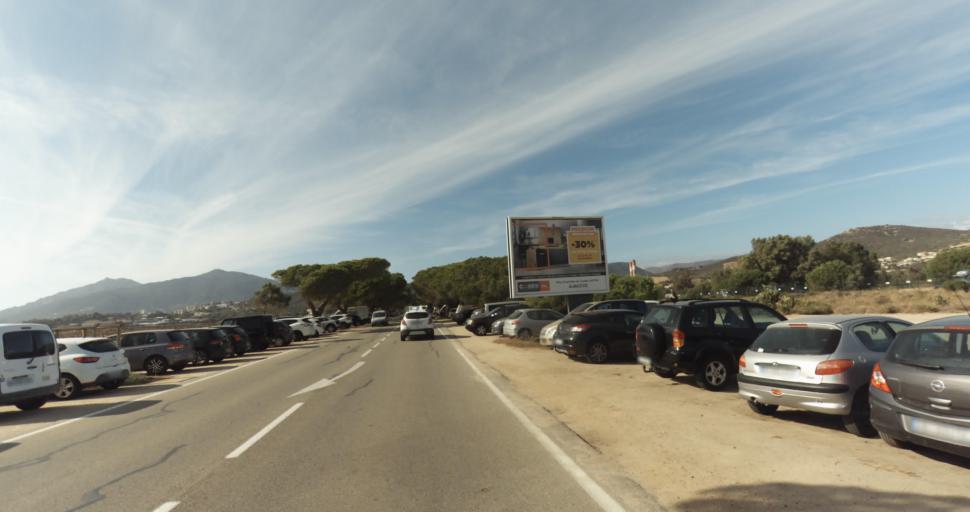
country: FR
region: Corsica
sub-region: Departement de la Corse-du-Sud
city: Ajaccio
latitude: 41.9223
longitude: 8.7858
